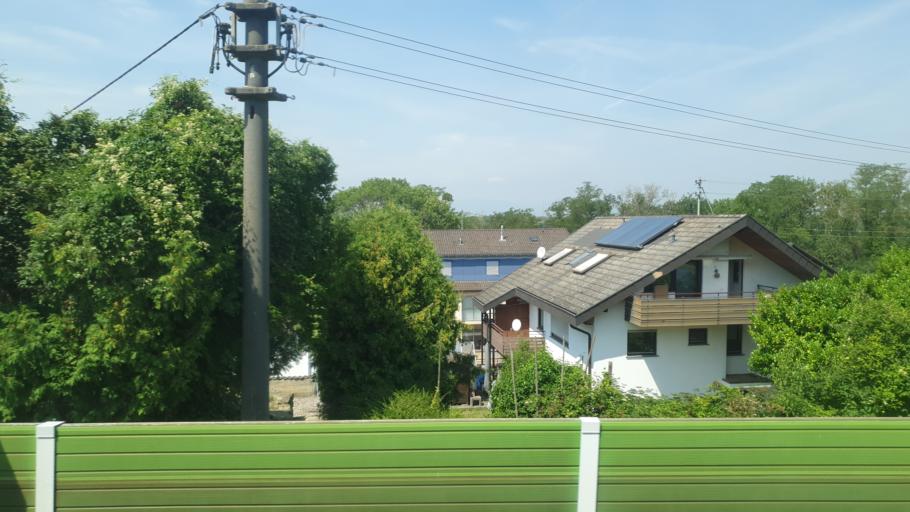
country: DE
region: Baden-Wuerttemberg
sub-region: Freiburg Region
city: Bad Bellingen
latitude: 47.7267
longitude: 7.5551
